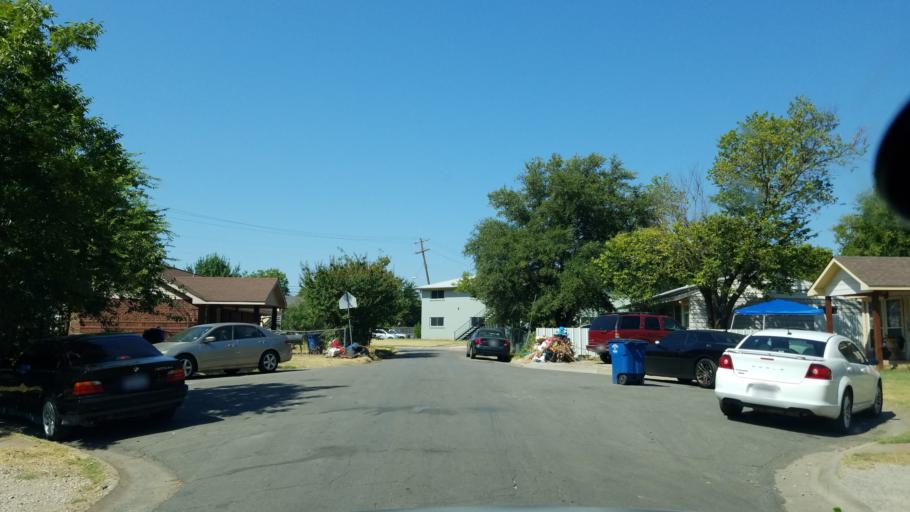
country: US
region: Texas
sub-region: Dallas County
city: Cockrell Hill
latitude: 32.7429
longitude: -96.8884
